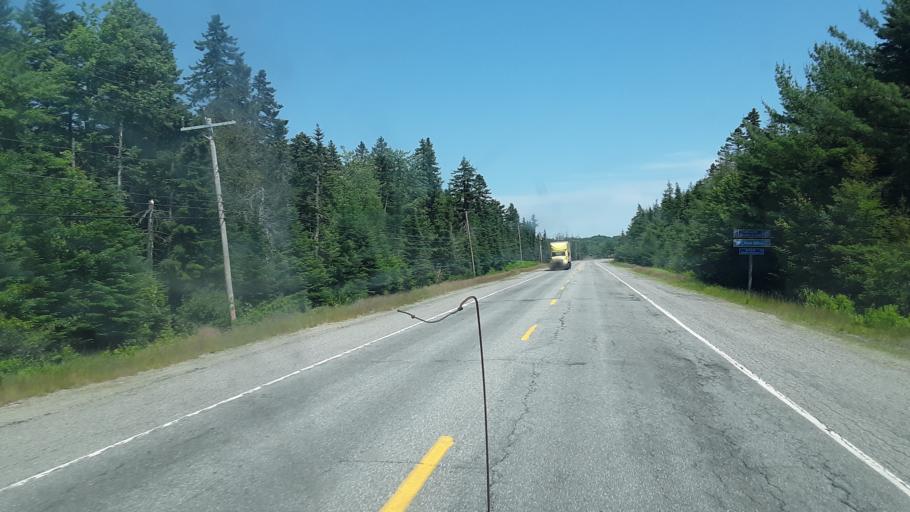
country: US
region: Maine
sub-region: Washington County
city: Steuben
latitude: 44.5121
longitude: -67.9727
